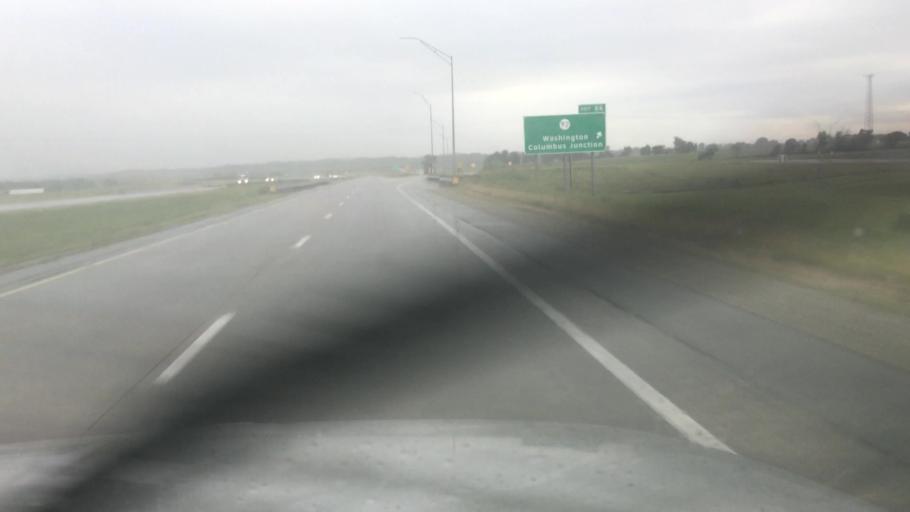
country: US
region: Iowa
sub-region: Washington County
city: Washington
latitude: 41.2929
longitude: -91.5344
